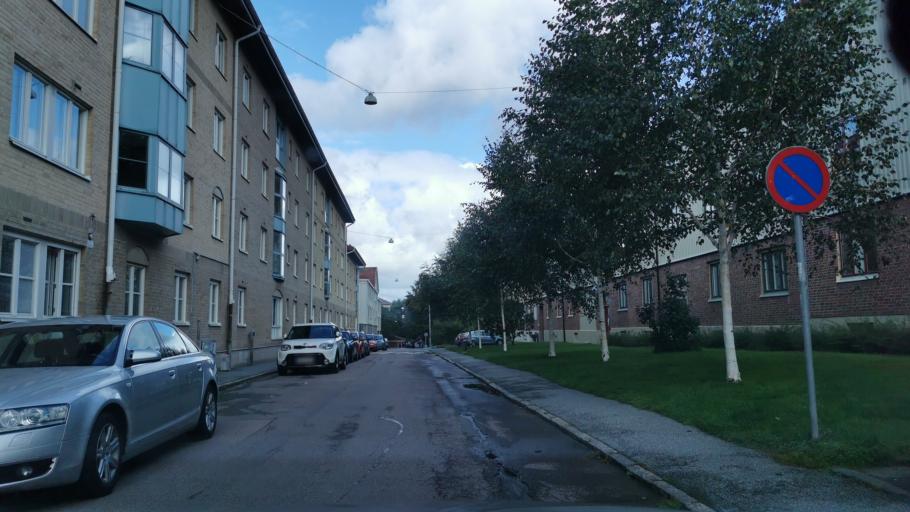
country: SE
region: Vaestra Goetaland
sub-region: Goteborg
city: Majorna
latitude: 57.6926
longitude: 11.9301
